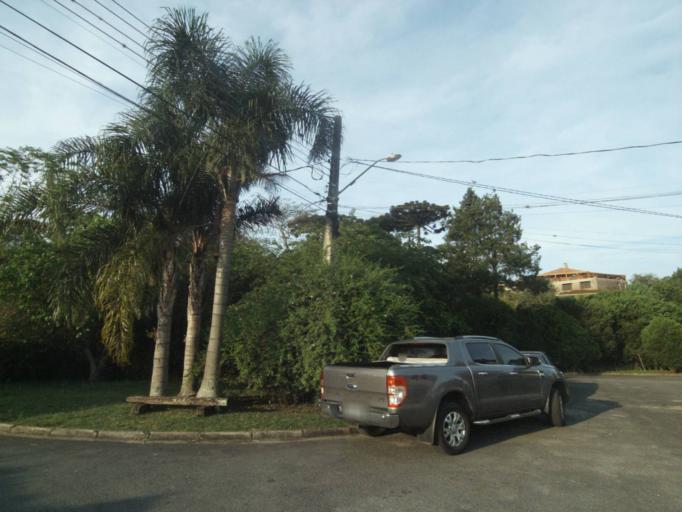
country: BR
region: Parana
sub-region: Curitiba
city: Curitiba
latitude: -25.4544
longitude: -49.3089
